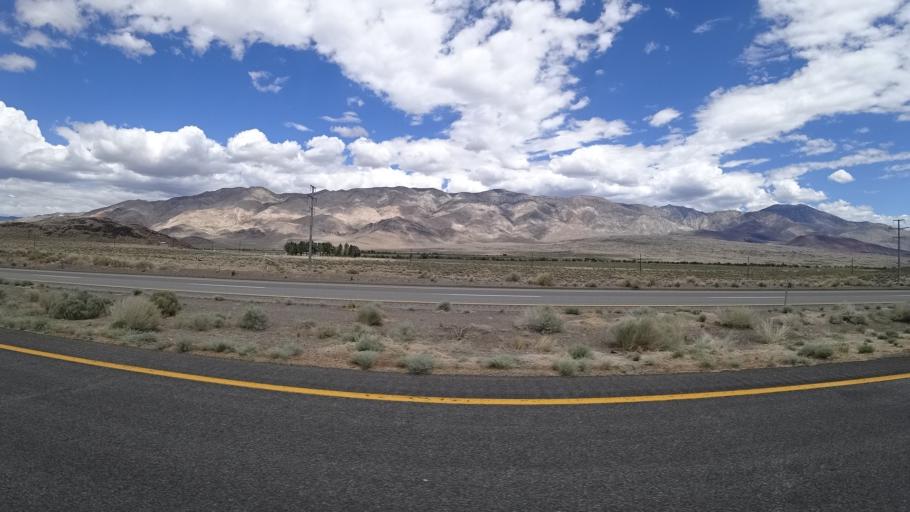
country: US
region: California
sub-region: Inyo County
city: Big Pine
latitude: 37.0510
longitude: -118.2338
